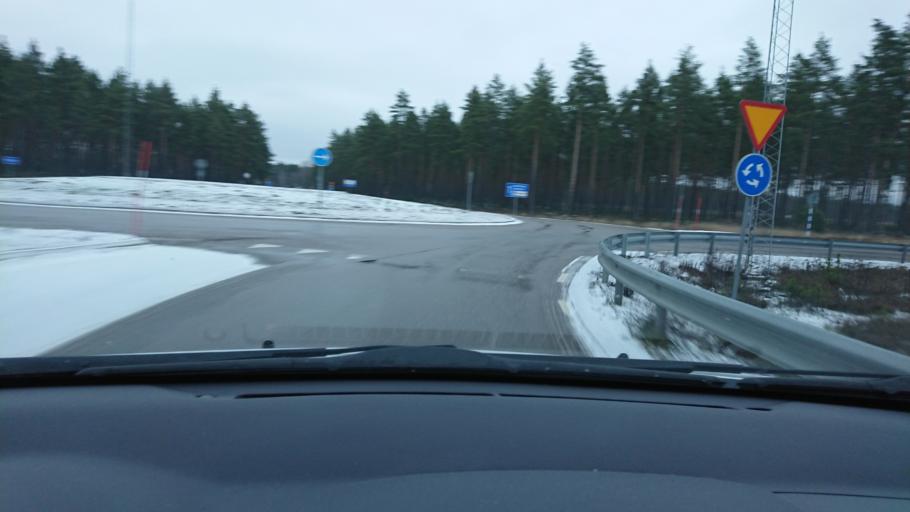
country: SE
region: Kalmar
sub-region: Hultsfreds Kommun
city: Hultsfred
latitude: 57.5105
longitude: 15.8359
